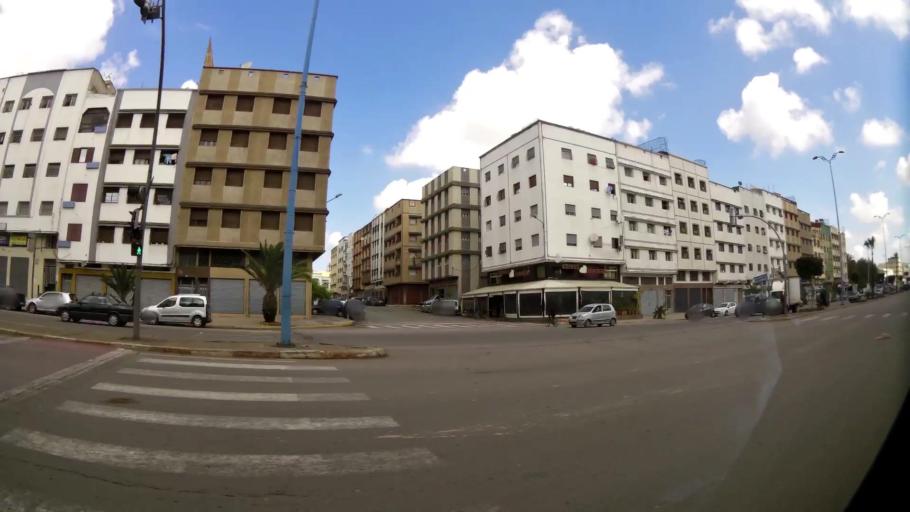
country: MA
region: Grand Casablanca
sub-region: Casablanca
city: Casablanca
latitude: 33.5369
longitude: -7.5735
